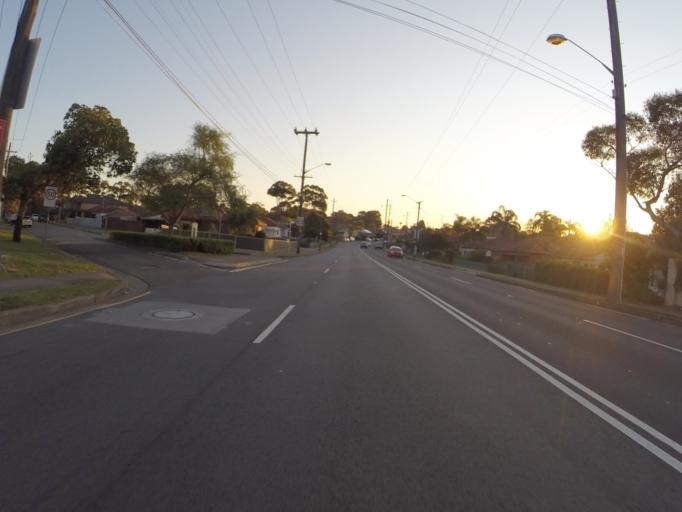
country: AU
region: New South Wales
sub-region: Hurstville
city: Penshurst
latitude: -33.9562
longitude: 151.0770
